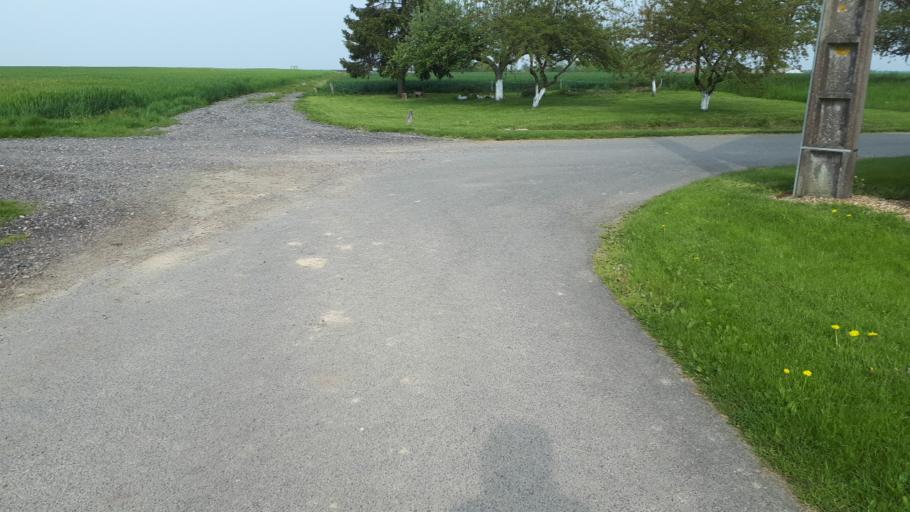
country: FR
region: Centre
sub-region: Departement du Loir-et-Cher
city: Lunay
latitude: 47.8353
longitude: 0.9466
